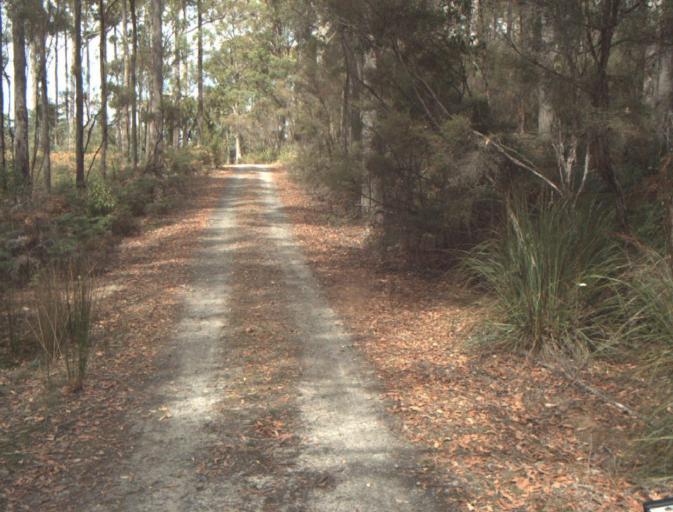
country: AU
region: Tasmania
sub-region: Launceston
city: Mayfield
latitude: -41.2008
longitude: 147.1642
